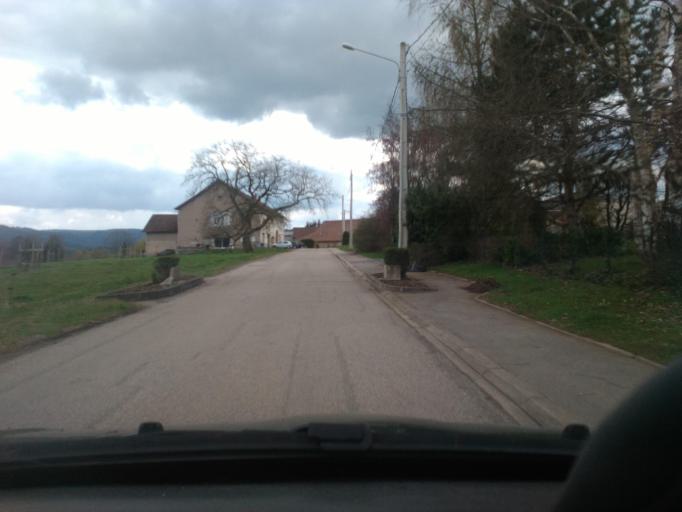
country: FR
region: Lorraine
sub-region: Departement des Vosges
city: Etival-Clairefontaine
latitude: 48.3488
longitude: 6.8321
